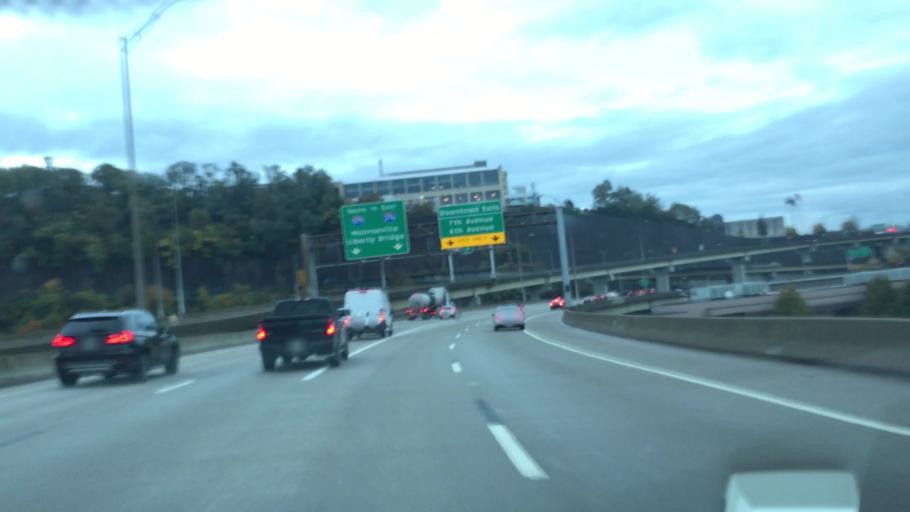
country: US
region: Pennsylvania
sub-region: Allegheny County
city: Pittsburgh
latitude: 40.4477
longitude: -79.9913
